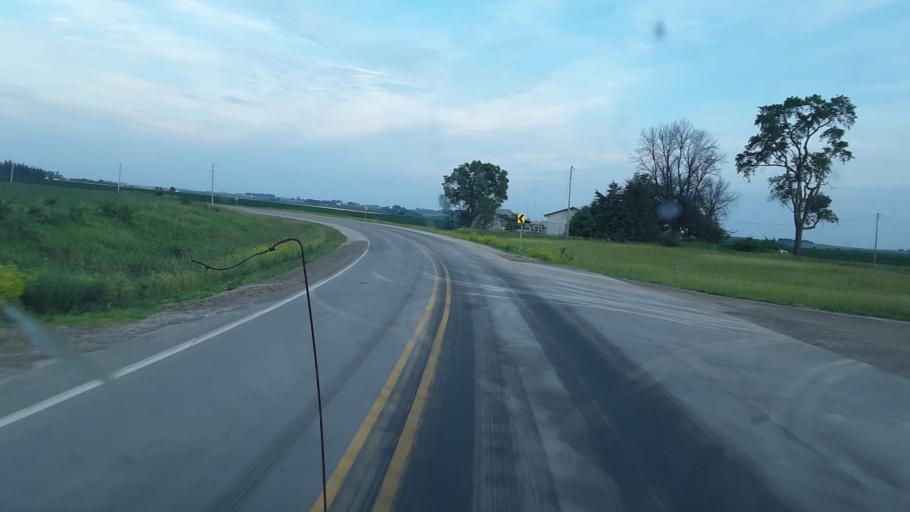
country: US
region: Iowa
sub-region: Iowa County
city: Marengo
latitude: 41.7044
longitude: -92.1824
